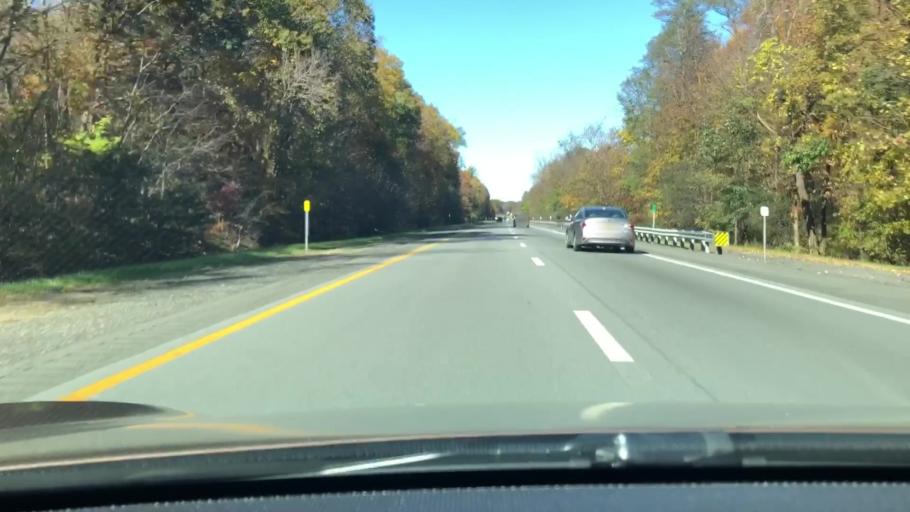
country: US
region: New York
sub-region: Orange County
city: Vails Gate
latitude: 41.4721
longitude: -74.0736
